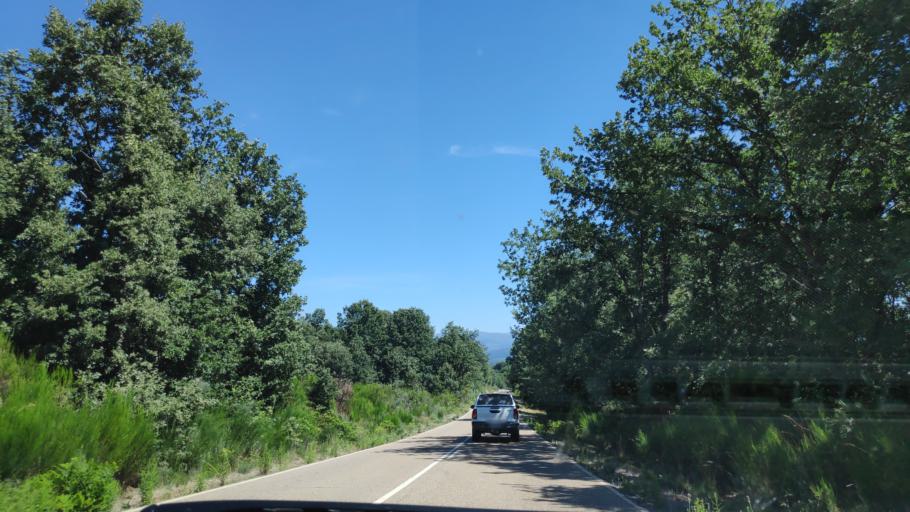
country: ES
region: Castille and Leon
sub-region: Provincia de Zamora
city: Cobreros
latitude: 42.0302
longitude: -6.6782
